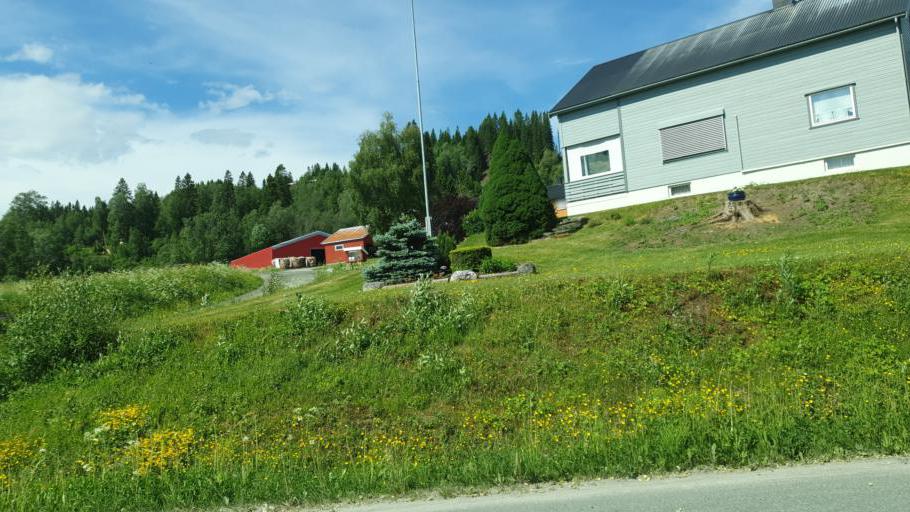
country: NO
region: Nord-Trondelag
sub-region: Leksvik
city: Leksvik
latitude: 63.6923
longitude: 10.6795
